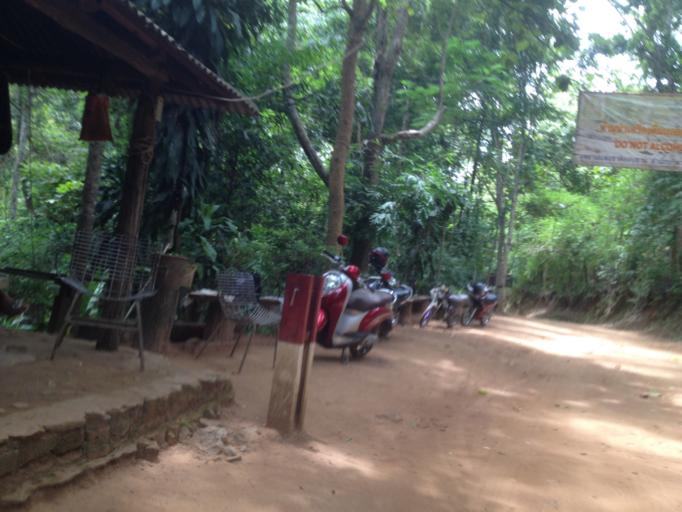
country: TH
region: Chiang Mai
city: Hang Dong
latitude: 18.7189
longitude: 98.8290
